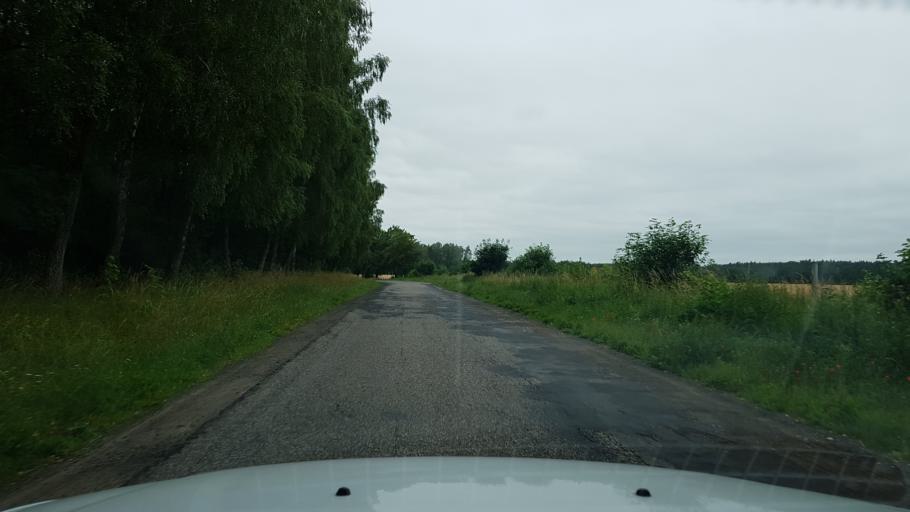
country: PL
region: West Pomeranian Voivodeship
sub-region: Powiat gryficki
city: Brojce
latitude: 53.9482
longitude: 15.3881
